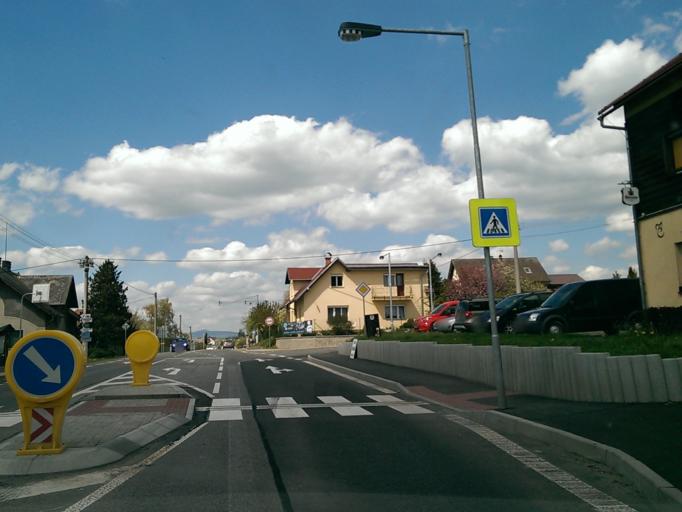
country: CZ
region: Liberecky
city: Rovensko pod Troskami
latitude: 50.5499
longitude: 15.2153
